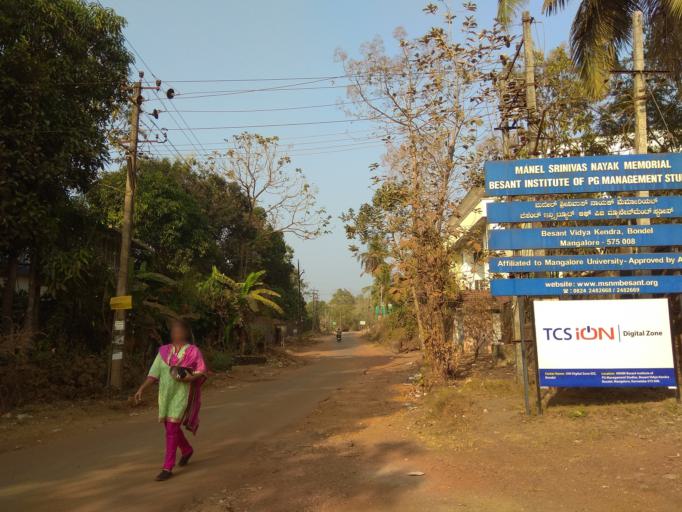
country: IN
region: Karnataka
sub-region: Dakshina Kannada
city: Mangalore
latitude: 12.9250
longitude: 74.8698
